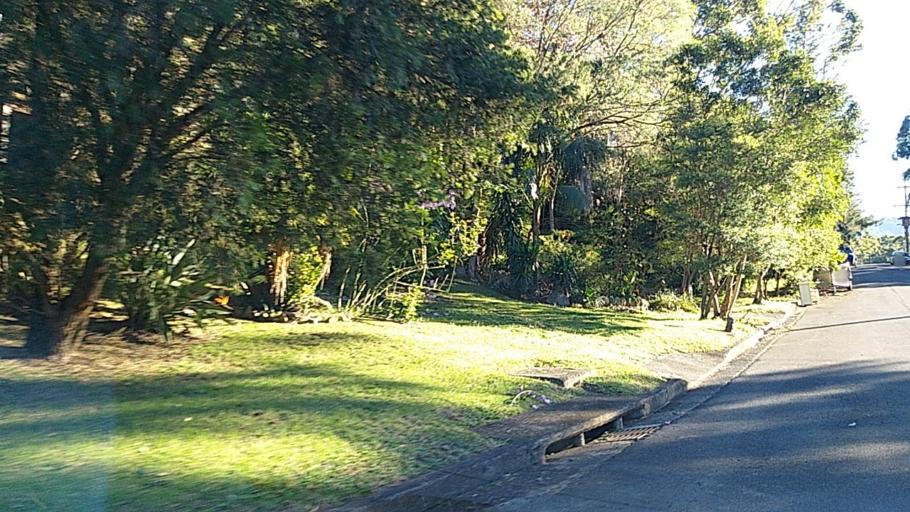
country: AU
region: New South Wales
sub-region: Wollongong
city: Bulli
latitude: -34.3251
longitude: 150.9041
